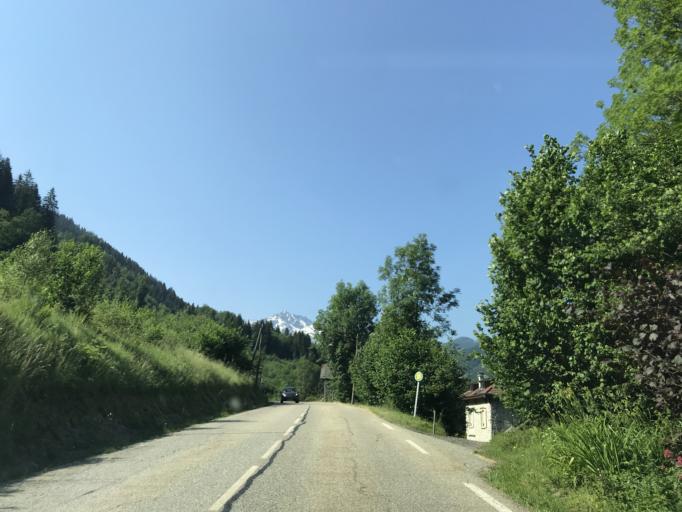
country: FR
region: Rhone-Alpes
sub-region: Departement de l'Isere
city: Allevard
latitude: 45.3269
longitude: 6.0904
